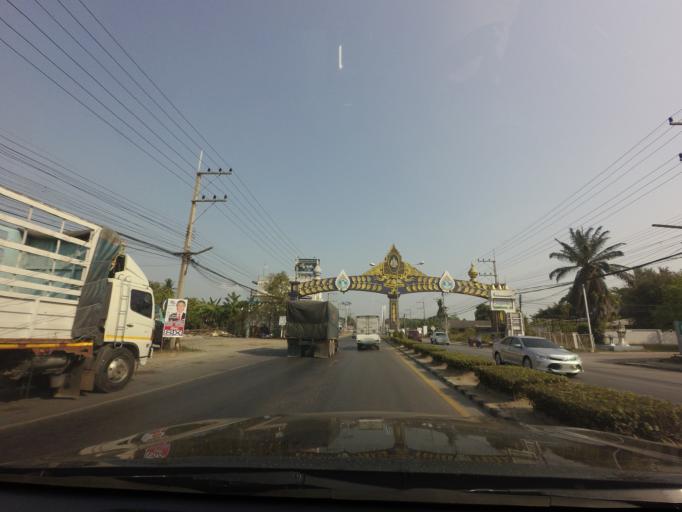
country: TH
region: Kanchanaburi
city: Tha Maka
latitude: 13.8685
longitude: 99.8220
